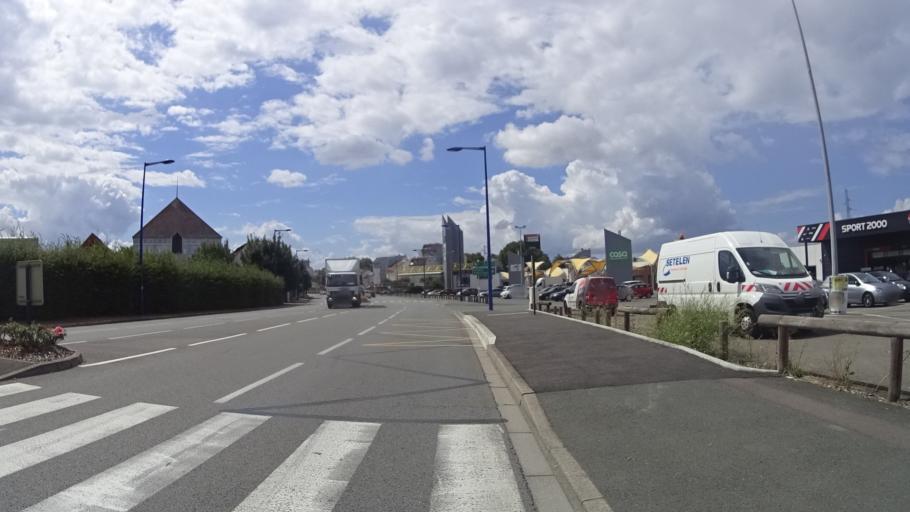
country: FR
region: Bourgogne
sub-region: Departement de Saone-et-Loire
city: Montceau-les-Mines
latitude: 46.6799
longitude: 4.3678
